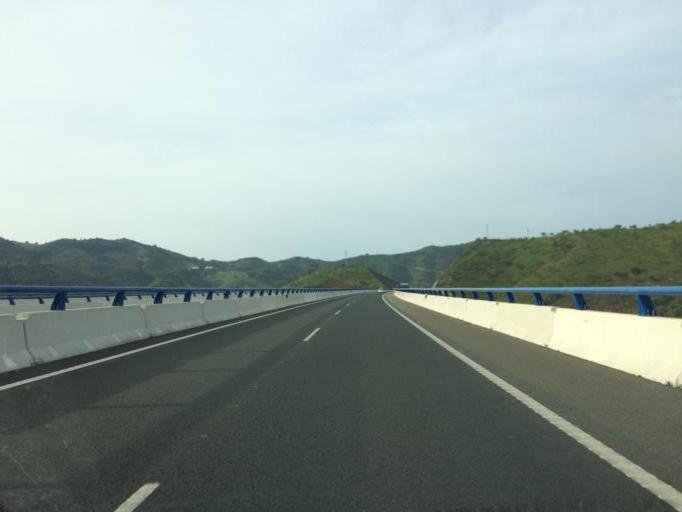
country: ES
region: Andalusia
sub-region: Provincia de Malaga
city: Casabermeja
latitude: 36.8882
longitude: -4.4696
